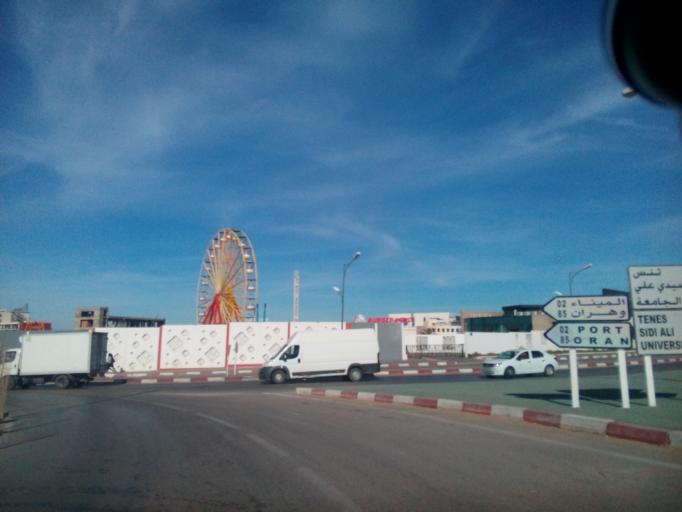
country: DZ
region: Mostaganem
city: Mostaganem
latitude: 35.9506
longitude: 0.0916
